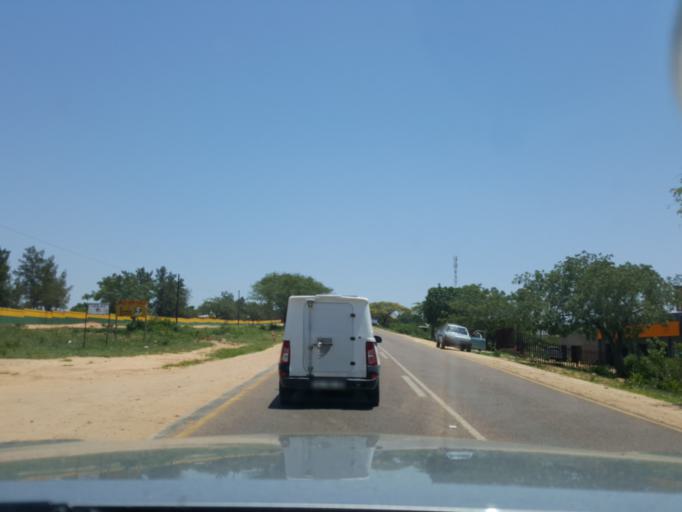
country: ZA
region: Limpopo
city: Thulamahashi
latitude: -24.6299
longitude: 31.0409
